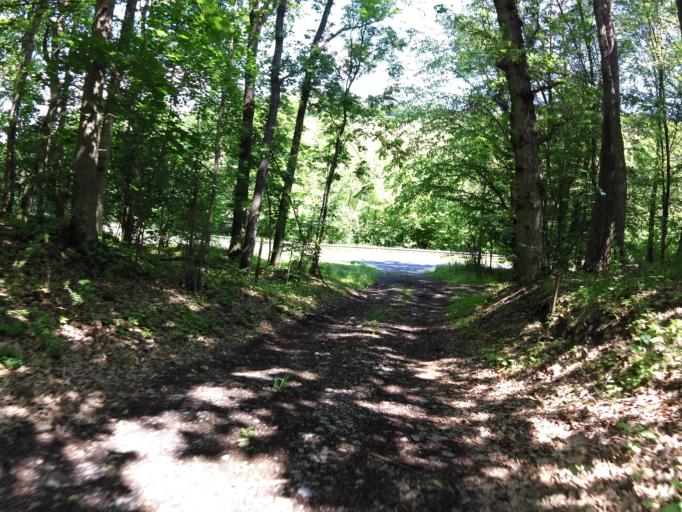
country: DE
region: Bavaria
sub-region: Regierungsbezirk Unterfranken
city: Eibelstadt
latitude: 49.7314
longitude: 10.0152
